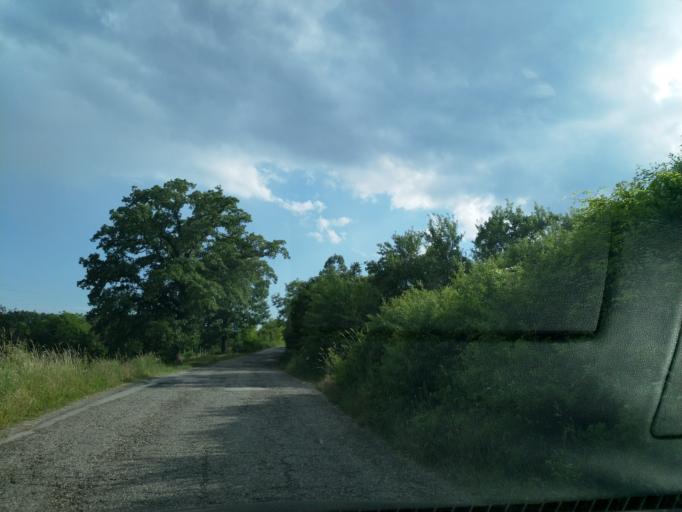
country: RS
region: Central Serbia
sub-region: Borski Okrug
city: Bor
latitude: 43.9929
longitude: 21.9778
